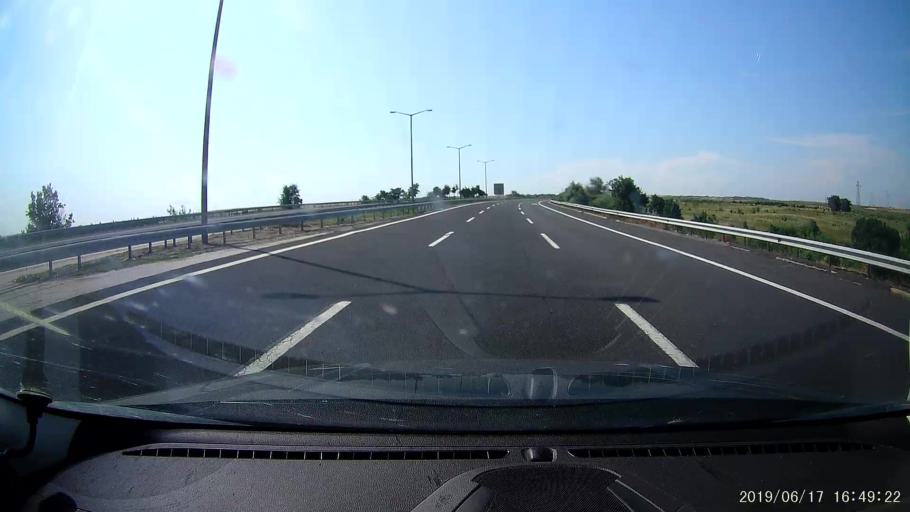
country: TR
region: Kirklareli
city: Babaeski
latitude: 41.5074
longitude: 27.1141
